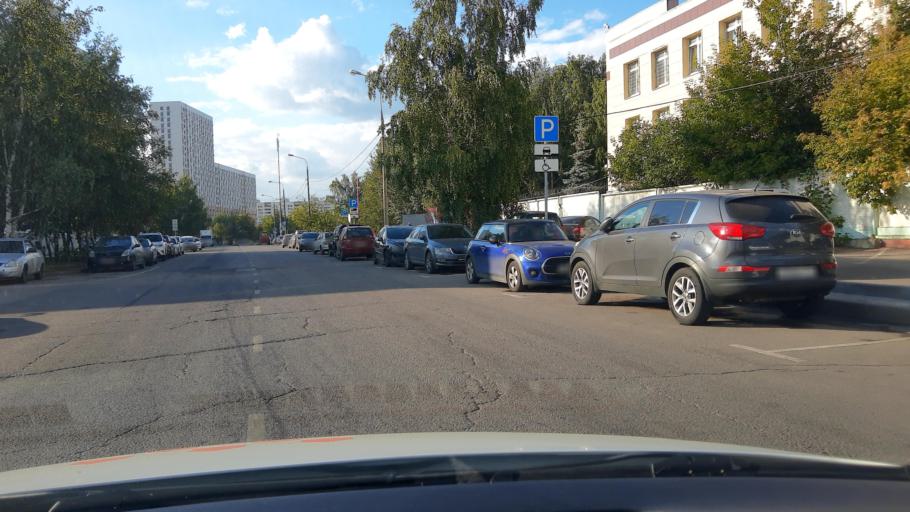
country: RU
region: Moskovskaya
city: Razvilka
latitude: 55.5992
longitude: 37.7388
